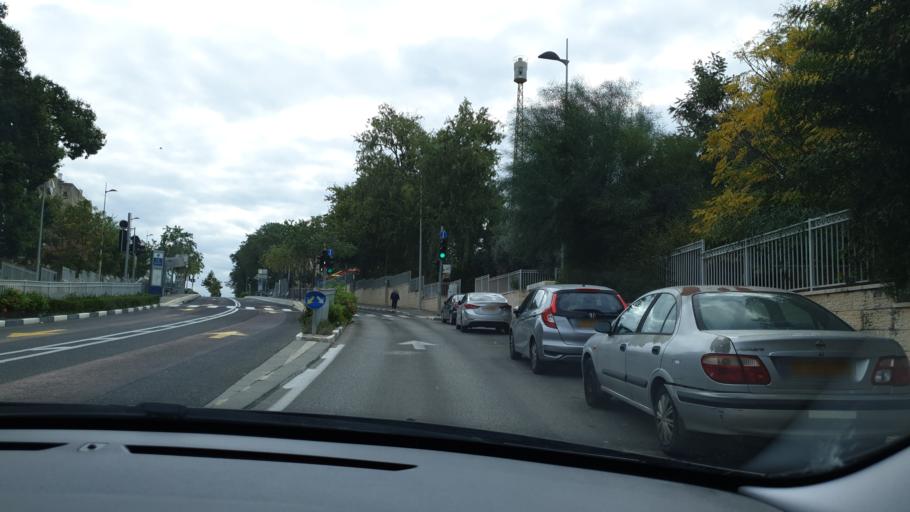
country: IL
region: Haifa
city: Qiryat Ata
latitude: 32.8112
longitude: 35.1146
